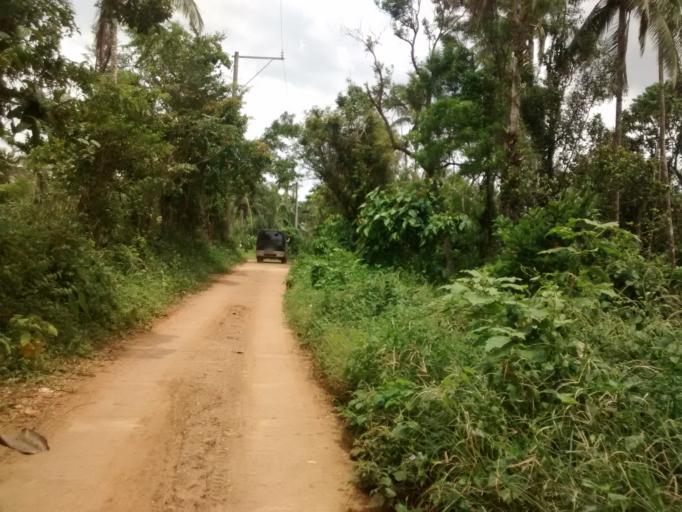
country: PH
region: Calabarzon
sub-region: Province of Quezon
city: Lucban
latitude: 14.1535
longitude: 121.5581
